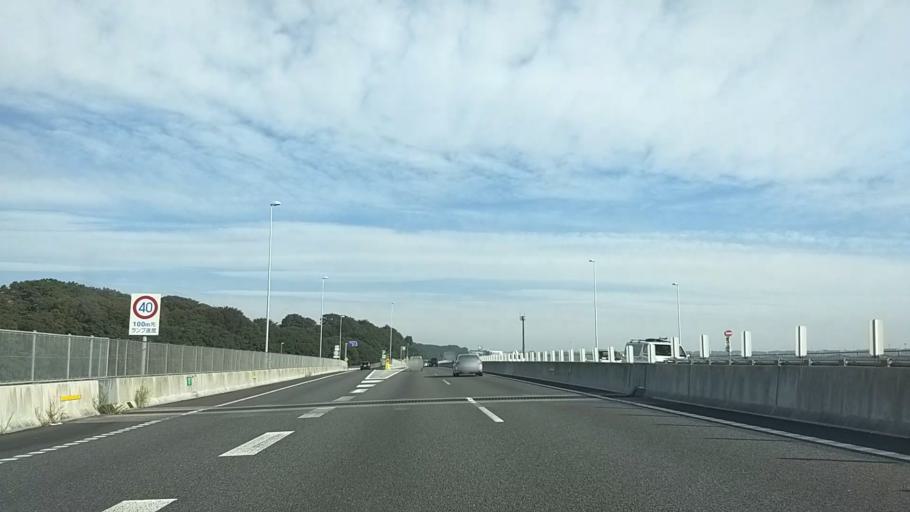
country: JP
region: Kanagawa
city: Zama
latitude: 35.4873
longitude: 139.3701
